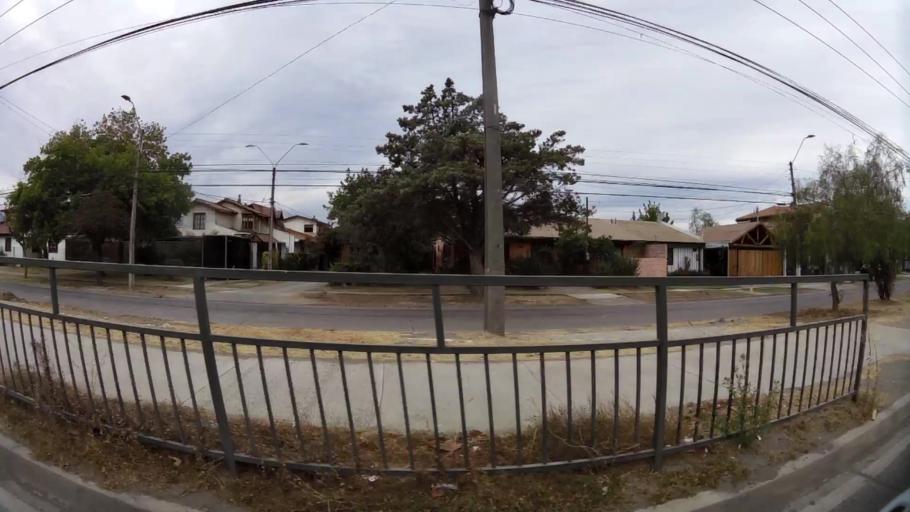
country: CL
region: O'Higgins
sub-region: Provincia de Cachapoal
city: Rancagua
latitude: -34.1433
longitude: -70.7389
